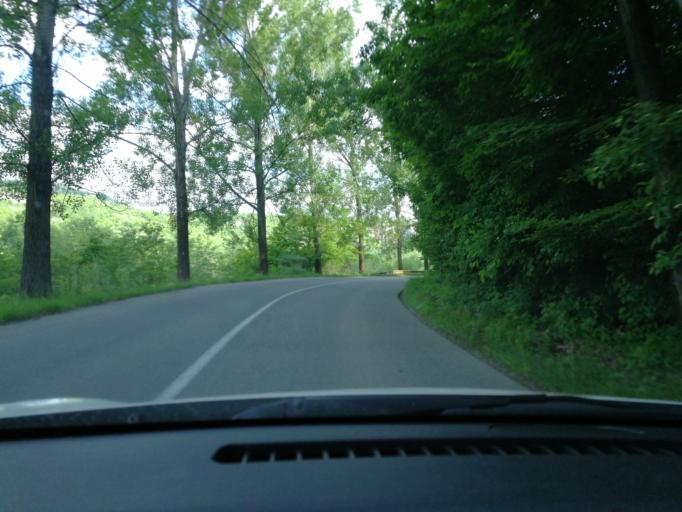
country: RO
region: Prahova
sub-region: Comuna Sotrile
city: Sotrile
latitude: 45.2163
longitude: 25.7381
